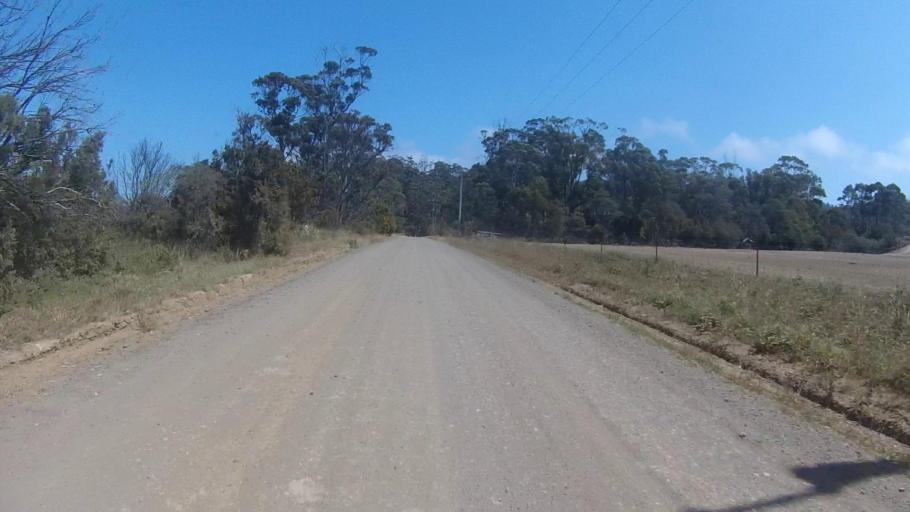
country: AU
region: Tasmania
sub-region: Sorell
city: Sorell
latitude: -42.8448
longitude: 147.8455
